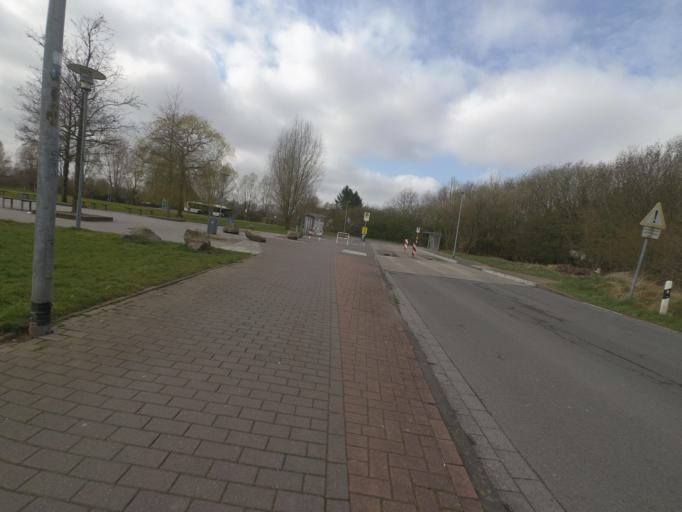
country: DE
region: Lower Saxony
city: Oldenburg
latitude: 53.1643
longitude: 8.1778
